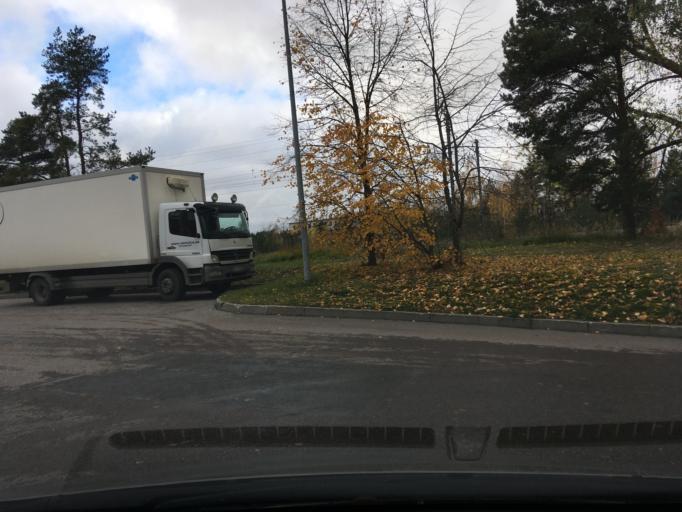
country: EE
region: Harju
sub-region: Tallinna linn
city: Tallinn
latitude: 59.3949
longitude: 24.7202
